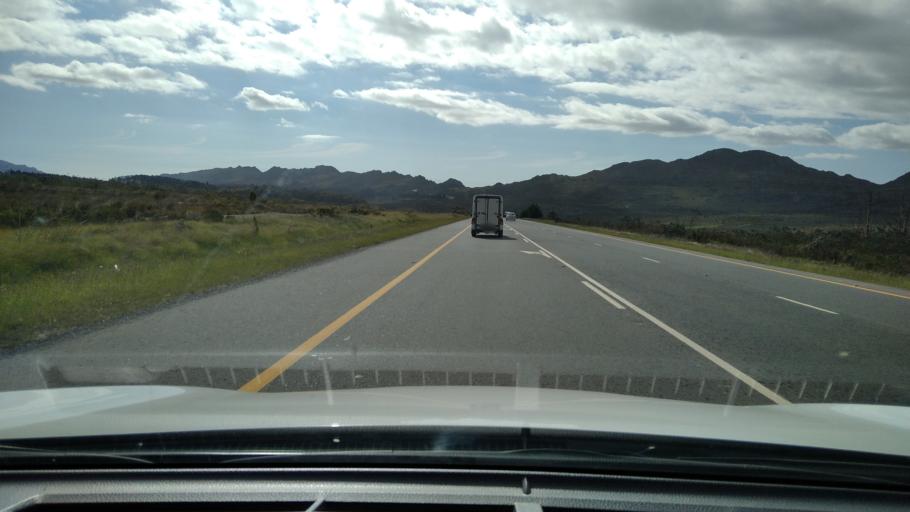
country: ZA
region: Western Cape
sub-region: Overberg District Municipality
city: Grabouw
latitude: -34.1525
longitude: 18.9622
